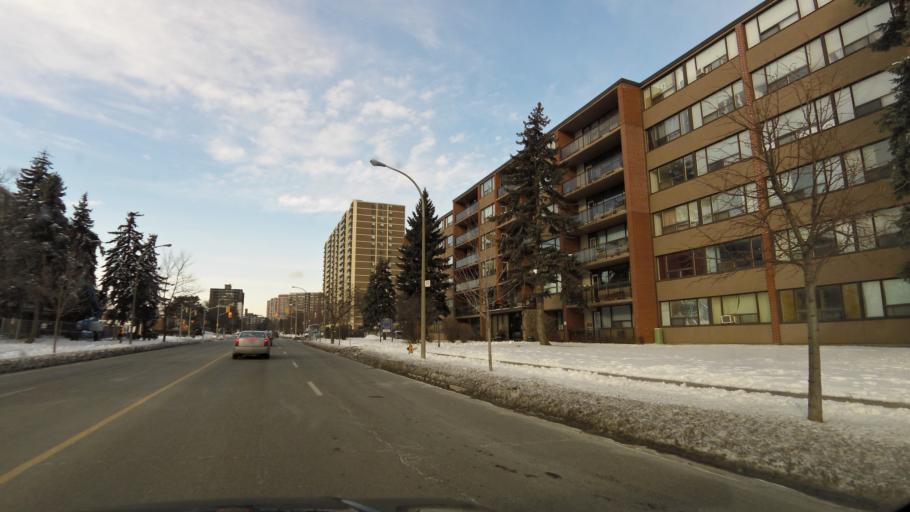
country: CA
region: Ontario
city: Etobicoke
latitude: 43.6485
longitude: -79.5683
